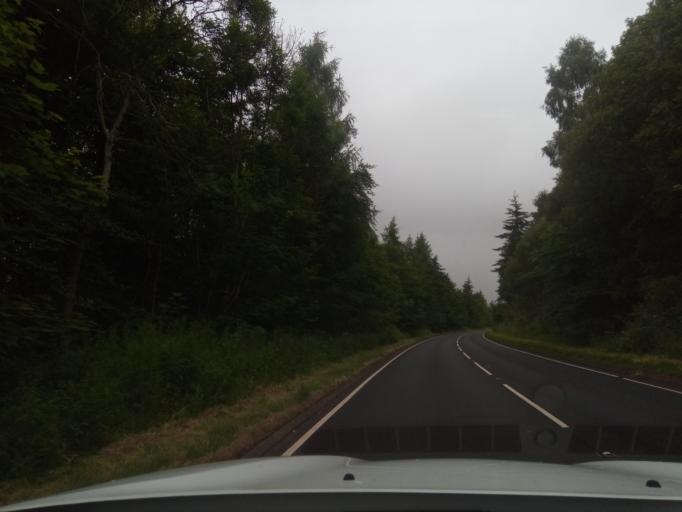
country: GB
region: Scotland
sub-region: The Scottish Borders
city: Earlston
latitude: 55.6615
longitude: -2.6950
